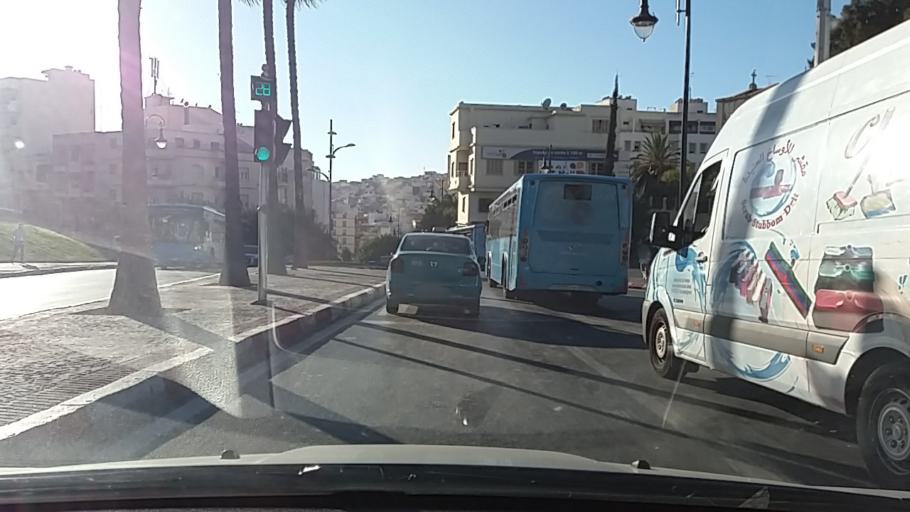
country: MA
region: Tanger-Tetouan
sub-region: Tanger-Assilah
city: Tangier
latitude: 35.7842
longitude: -5.8229
